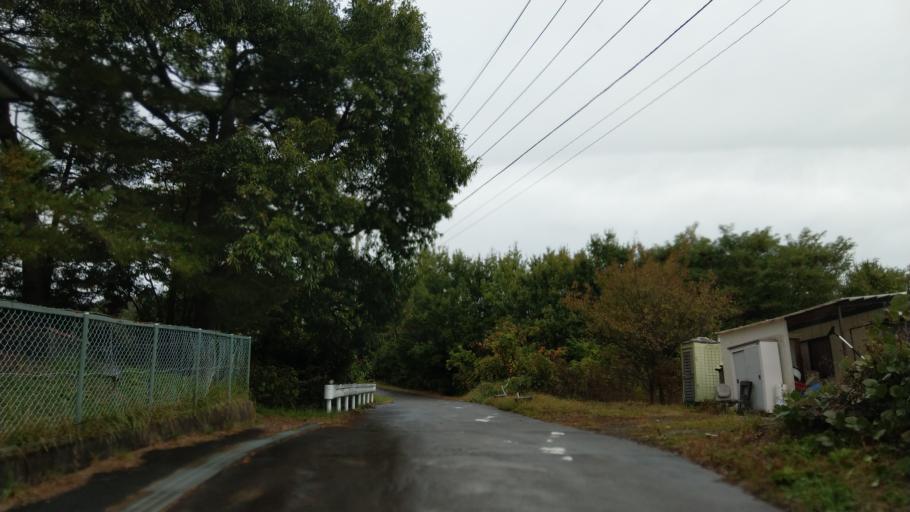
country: JP
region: Nagano
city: Komoro
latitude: 36.3581
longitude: 138.4247
